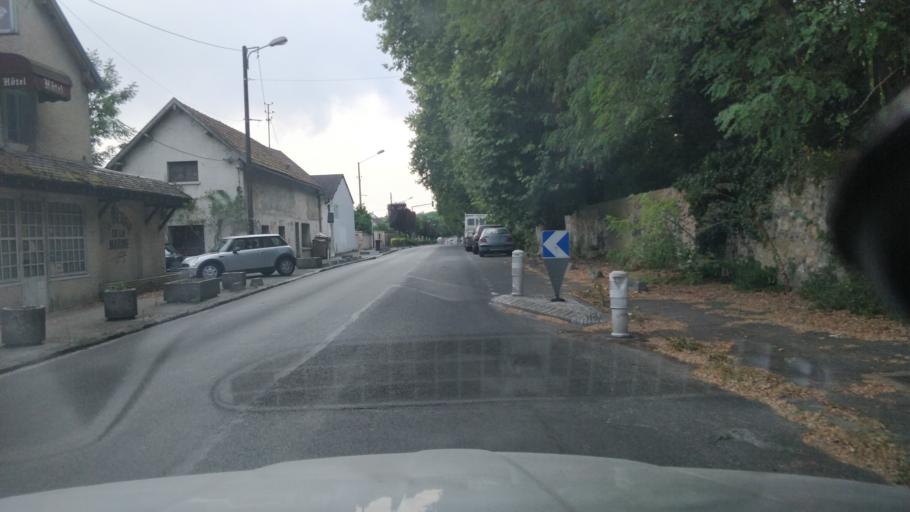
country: FR
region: Ile-de-France
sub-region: Departement de Seine-et-Marne
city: Pomponne
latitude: 48.8799
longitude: 2.6770
